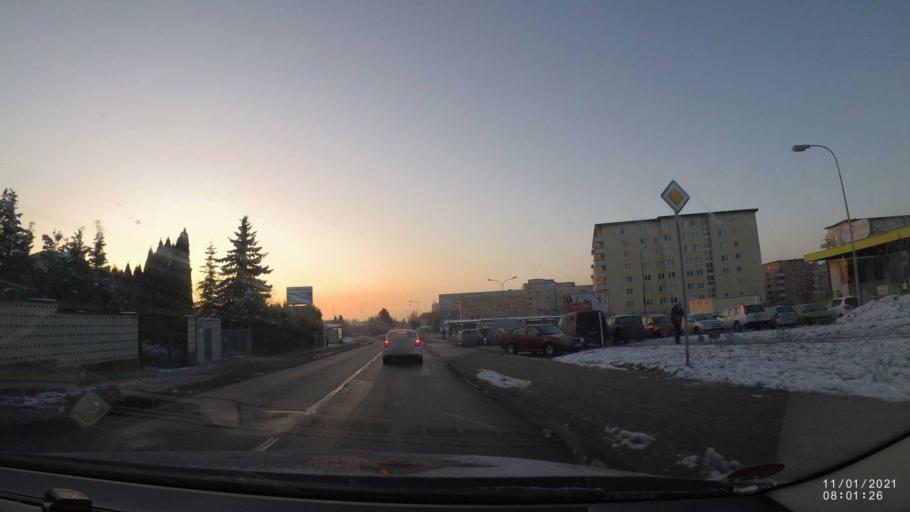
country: CZ
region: South Moravian
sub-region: Mesto Brno
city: Mokra Hora
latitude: 49.2369
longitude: 16.6272
